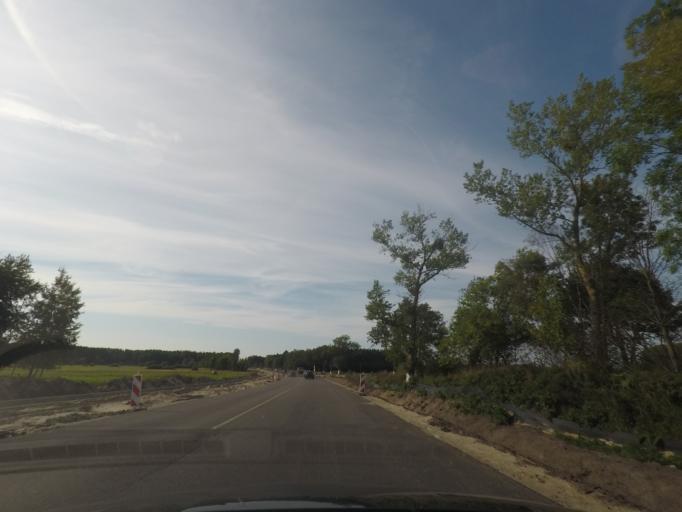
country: PL
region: Pomeranian Voivodeship
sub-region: Powiat leborski
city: Leba
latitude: 54.7279
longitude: 17.5683
